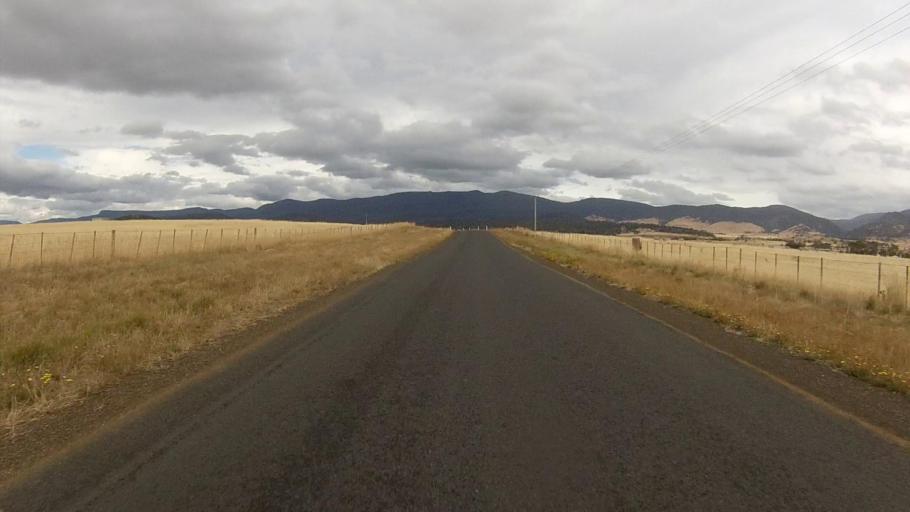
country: AU
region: Tasmania
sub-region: Northern Midlands
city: Evandale
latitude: -41.8216
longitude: 147.7582
